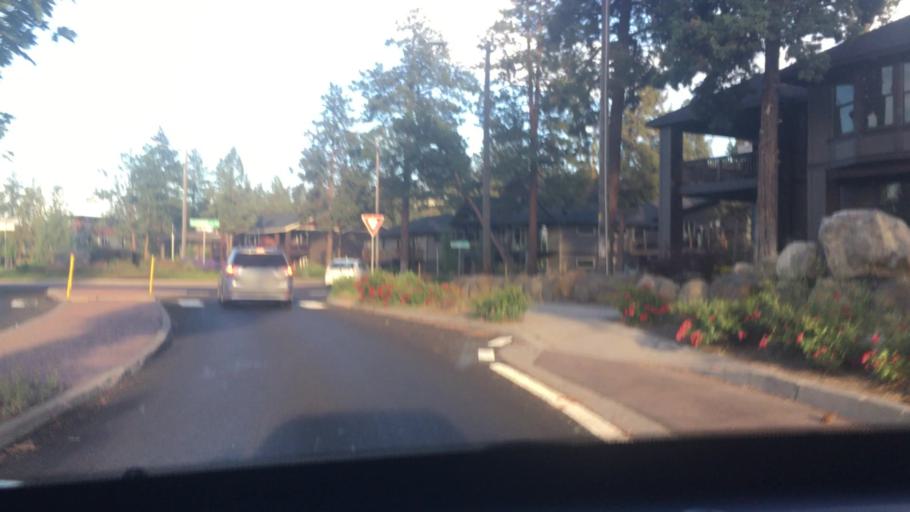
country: US
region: Oregon
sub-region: Deschutes County
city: Bend
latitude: 44.0406
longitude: -121.3224
